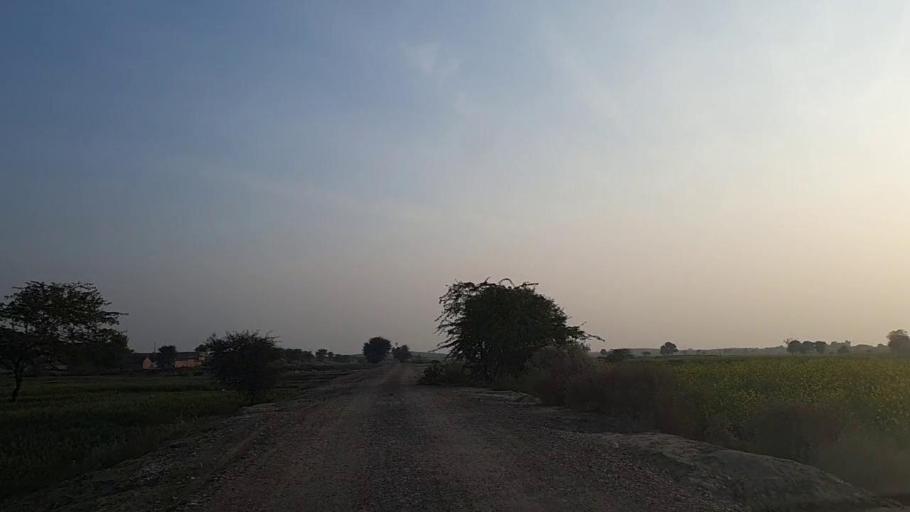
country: PK
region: Sindh
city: Jam Sahib
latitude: 26.4110
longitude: 68.6056
